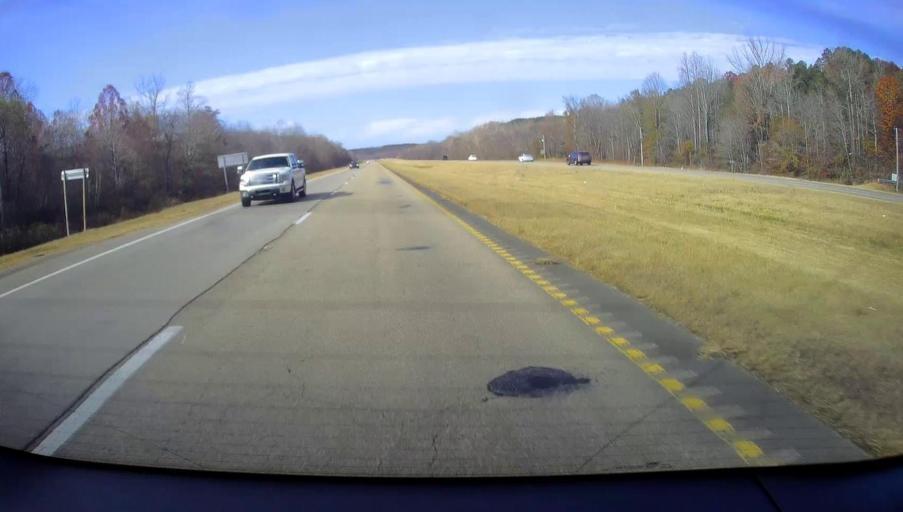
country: US
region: Mississippi
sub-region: Alcorn County
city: Corinth
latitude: 34.9371
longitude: -88.7759
